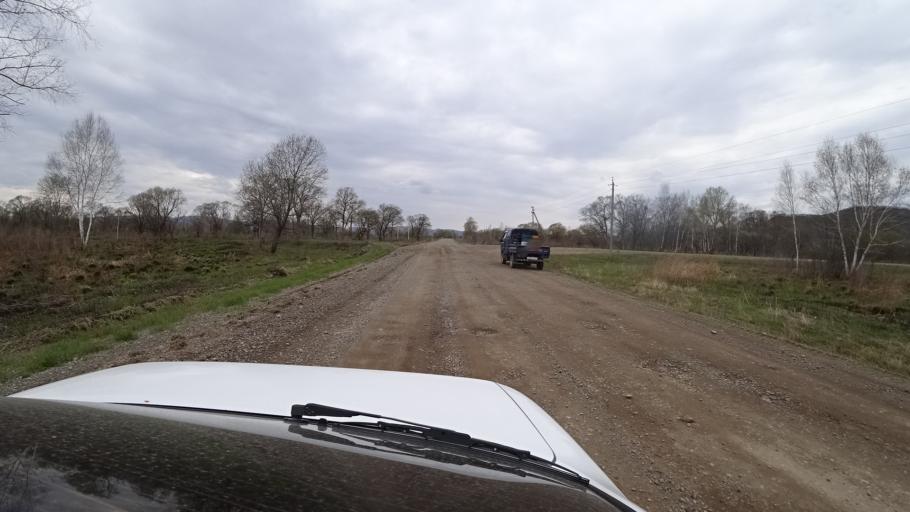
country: RU
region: Primorskiy
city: Novopokrovka
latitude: 45.5613
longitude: 134.3376
